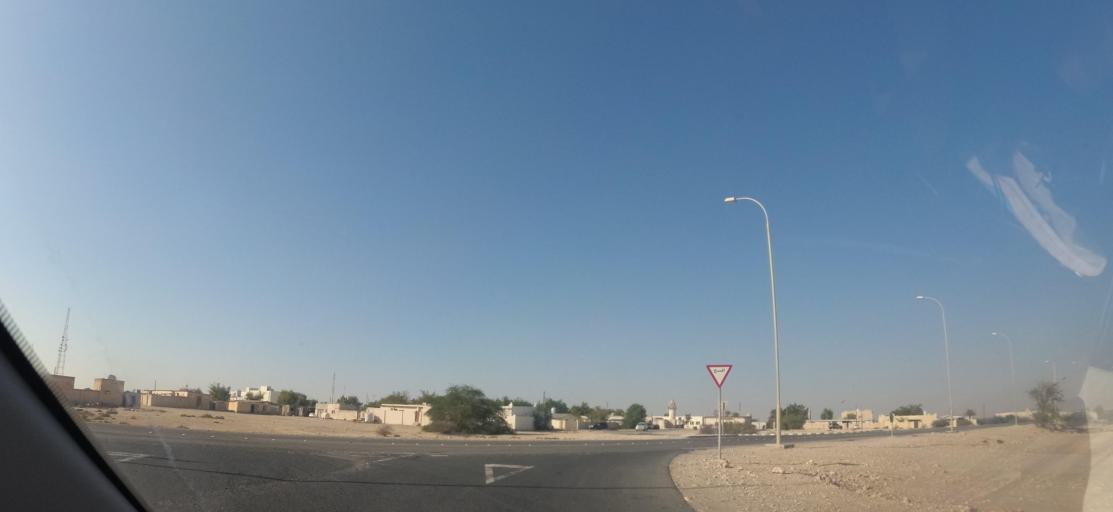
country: QA
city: Al Jumayliyah
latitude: 25.6189
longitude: 51.0857
